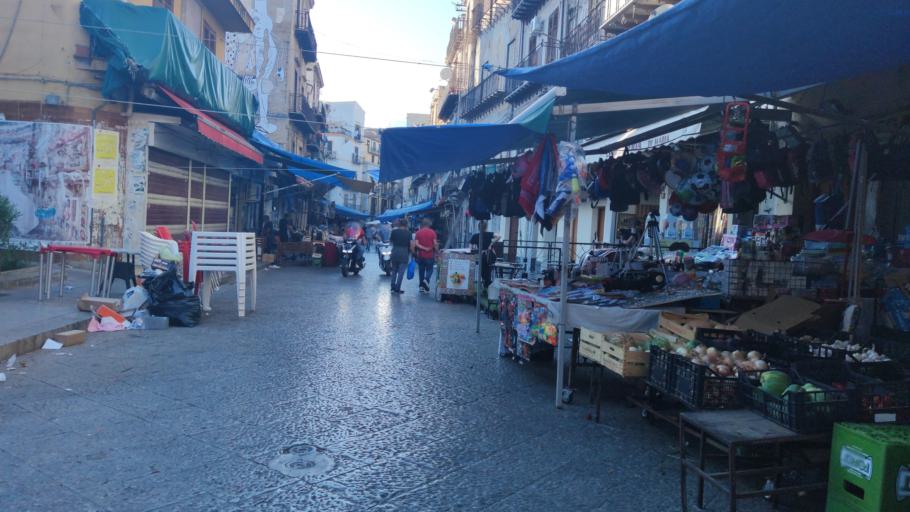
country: IT
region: Sicily
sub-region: Palermo
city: Palermo
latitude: 38.1118
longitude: 13.3609
